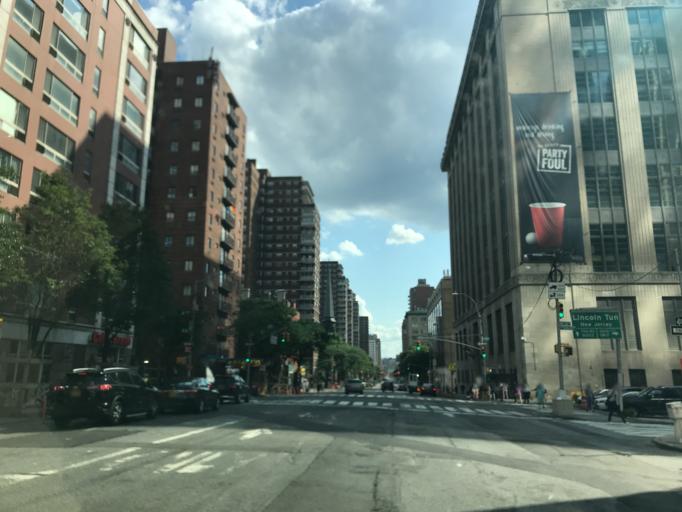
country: US
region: New Jersey
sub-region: Hudson County
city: Weehawken
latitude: 40.7513
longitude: -73.9979
